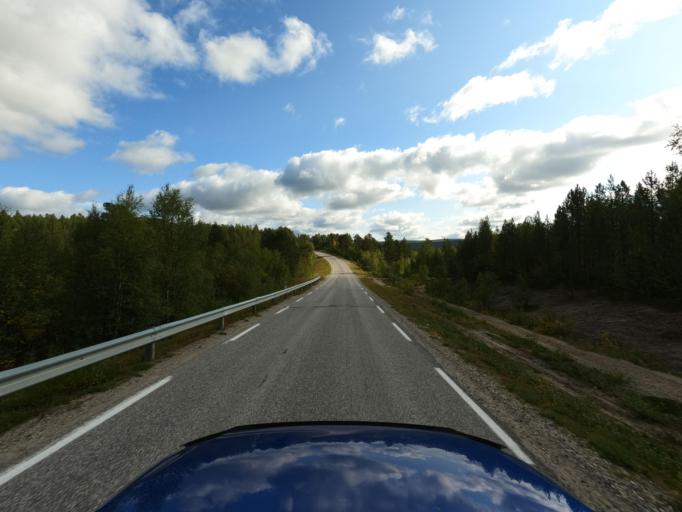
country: NO
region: Finnmark Fylke
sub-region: Karasjok
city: Karasjohka
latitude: 69.4430
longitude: 25.2695
